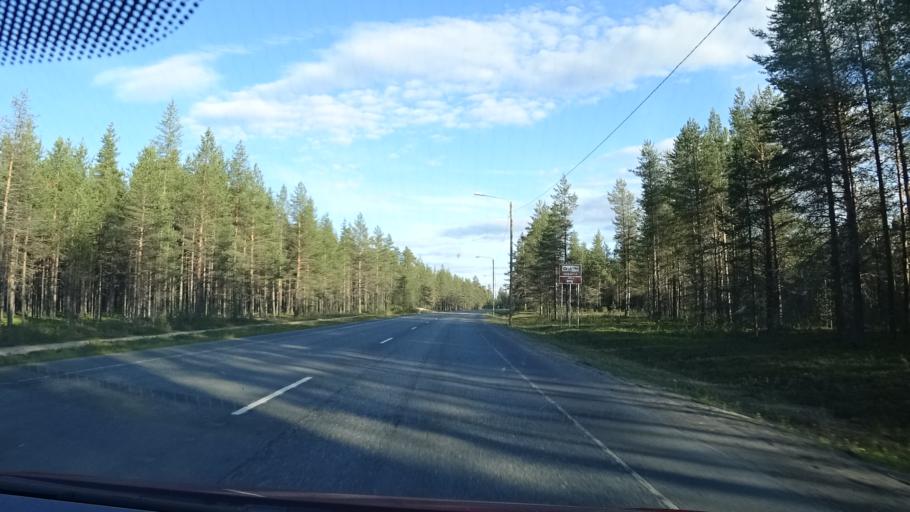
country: FI
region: Northern Ostrobothnia
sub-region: Koillismaa
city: Kuusamo
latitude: 66.0092
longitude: 29.1512
